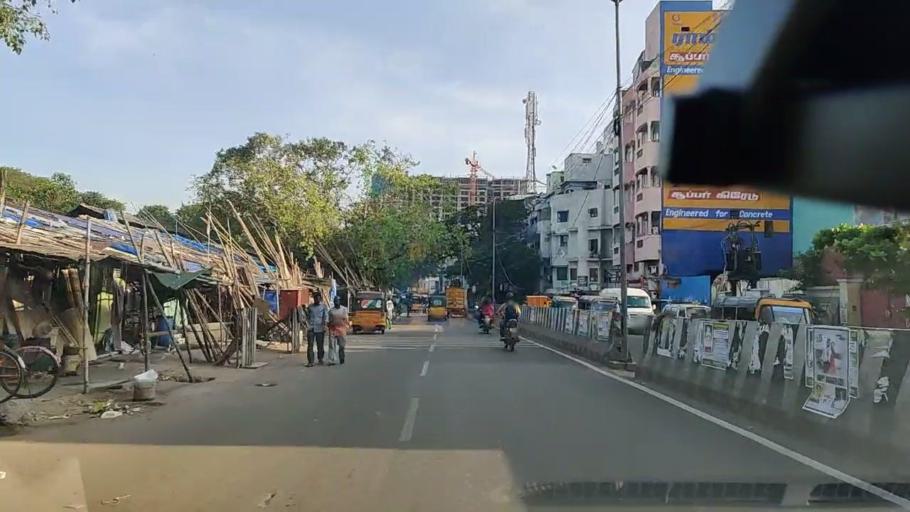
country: IN
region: Tamil Nadu
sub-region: Chennai
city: George Town
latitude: 13.0986
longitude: 80.2752
